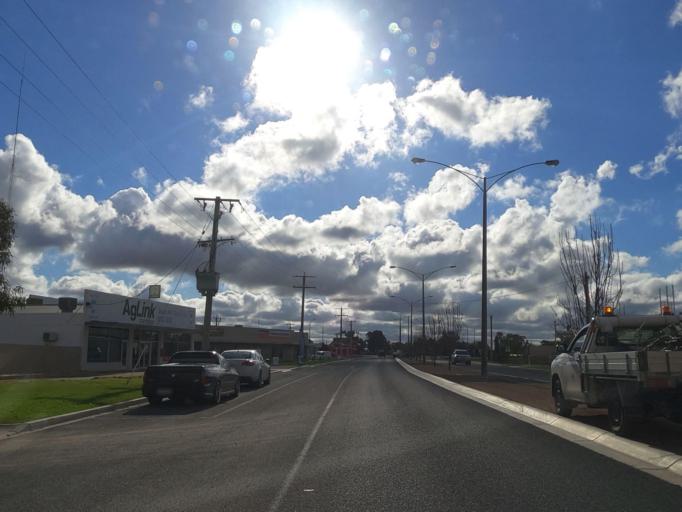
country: AU
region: Victoria
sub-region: Swan Hill
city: Swan Hill
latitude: -35.3295
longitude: 143.5541
